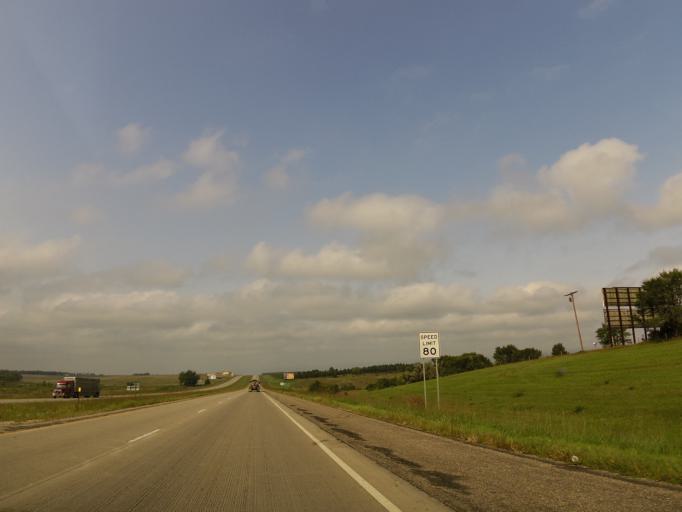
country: US
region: South Dakota
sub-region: Codington County
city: Watertown
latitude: 44.8981
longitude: -97.0565
